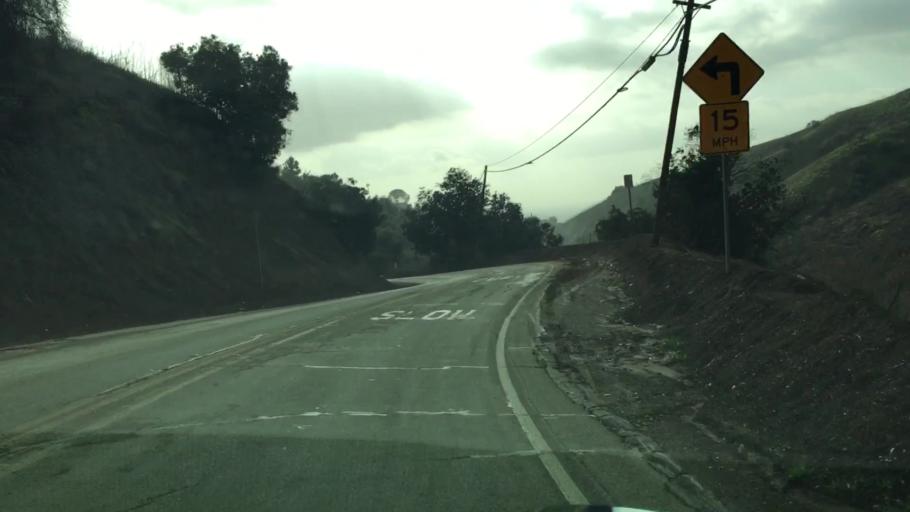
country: US
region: California
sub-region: Los Angeles County
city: Whittier
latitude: 33.9928
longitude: -118.0170
